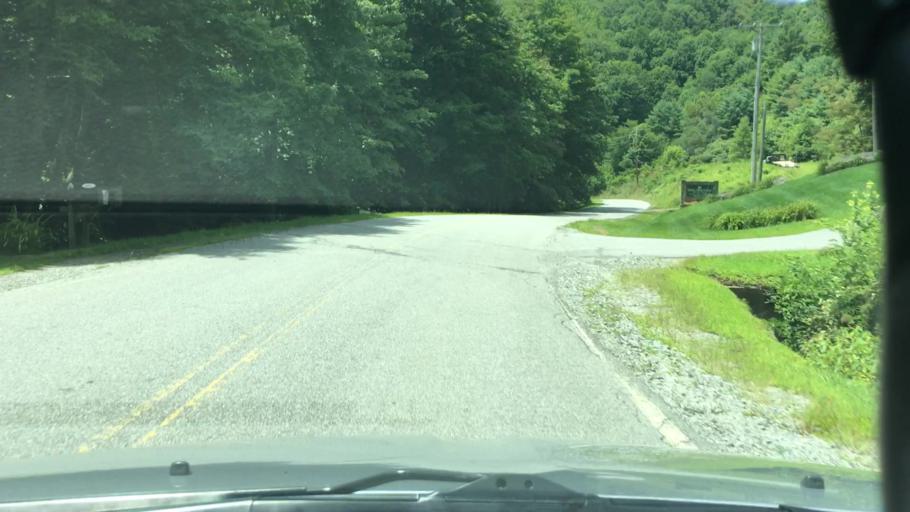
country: US
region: North Carolina
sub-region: Madison County
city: Mars Hill
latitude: 35.9505
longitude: -82.5199
